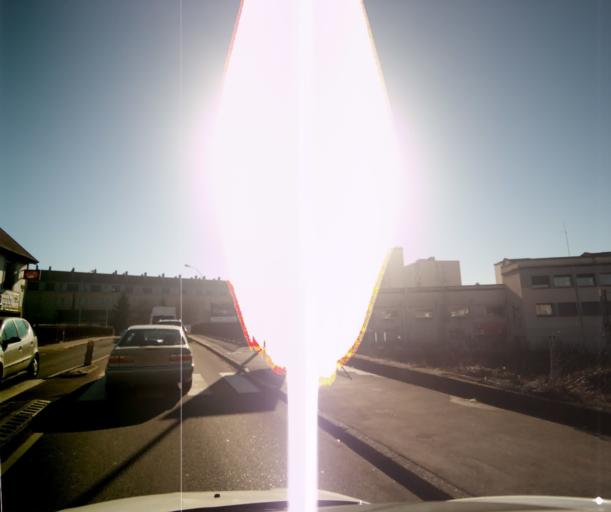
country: FR
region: Franche-Comte
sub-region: Departement du Doubs
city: Besancon
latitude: 47.2428
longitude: 6.0079
